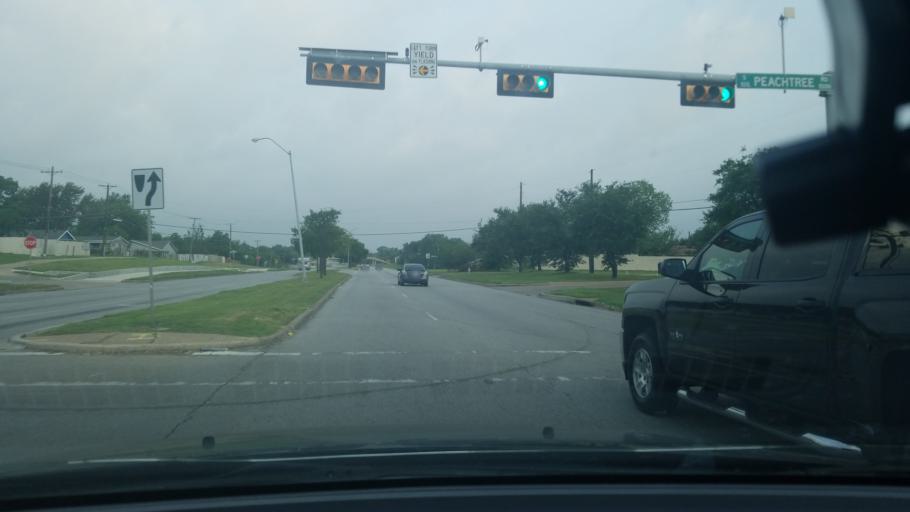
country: US
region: Texas
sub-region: Dallas County
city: Mesquite
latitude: 32.7682
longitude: -96.6299
